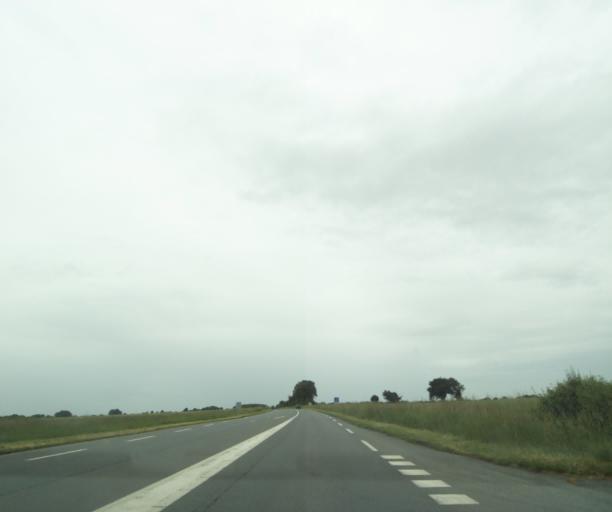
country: FR
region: Poitou-Charentes
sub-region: Departement des Deux-Sevres
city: Cherveux
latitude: 46.4319
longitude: -0.3910
